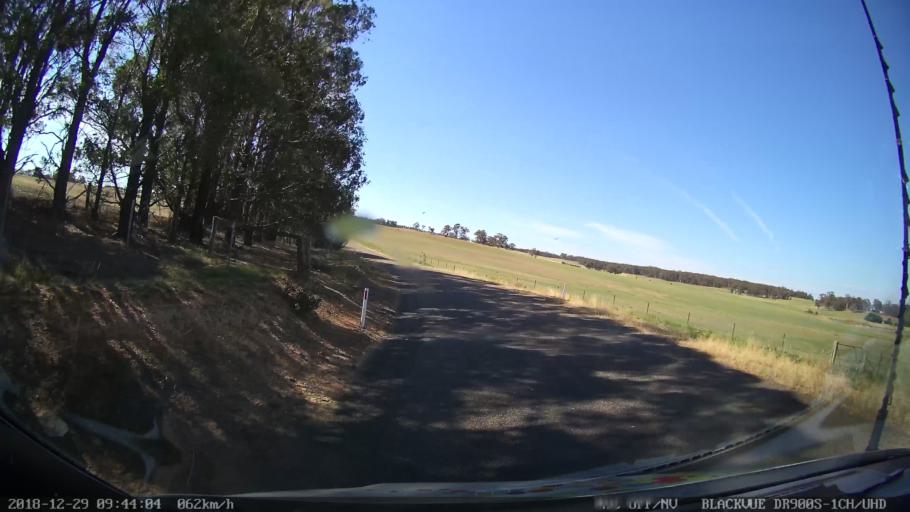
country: AU
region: New South Wales
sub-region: Upper Lachlan Shire
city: Crookwell
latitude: -34.6856
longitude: 149.4247
